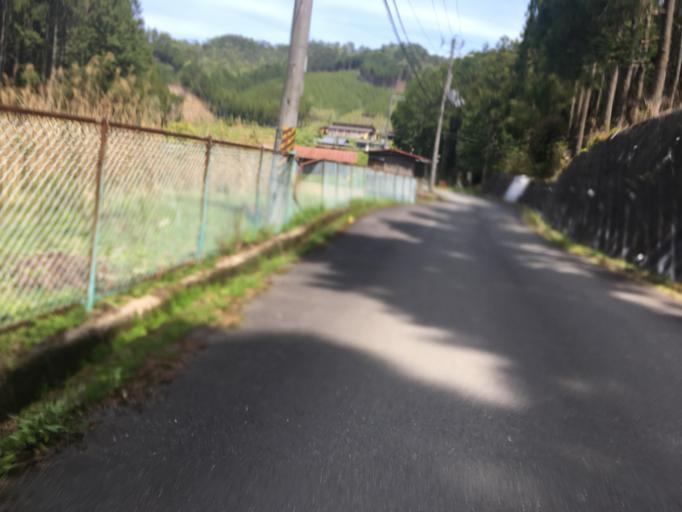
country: JP
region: Kyoto
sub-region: Kyoto-shi
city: Kamigyo-ku
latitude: 35.0829
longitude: 135.7220
